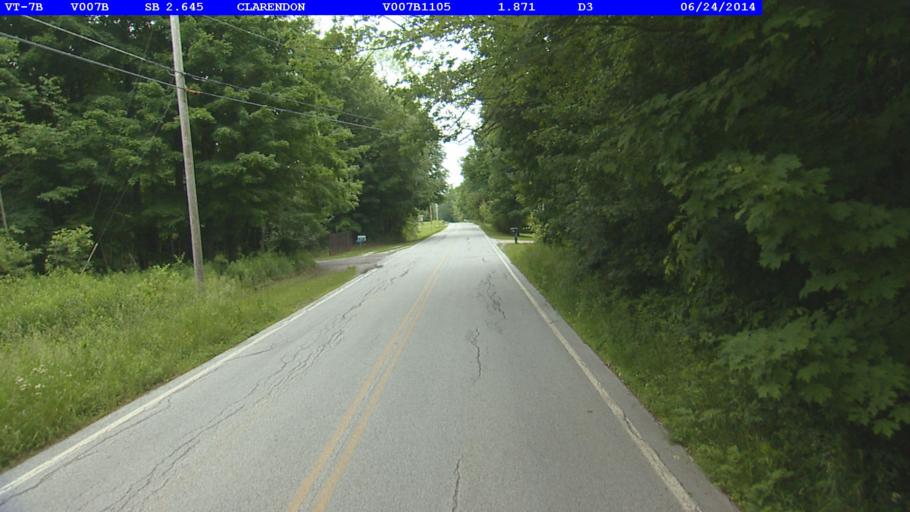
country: US
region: Vermont
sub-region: Rutland County
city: Rutland
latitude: 43.5274
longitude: -72.9576
